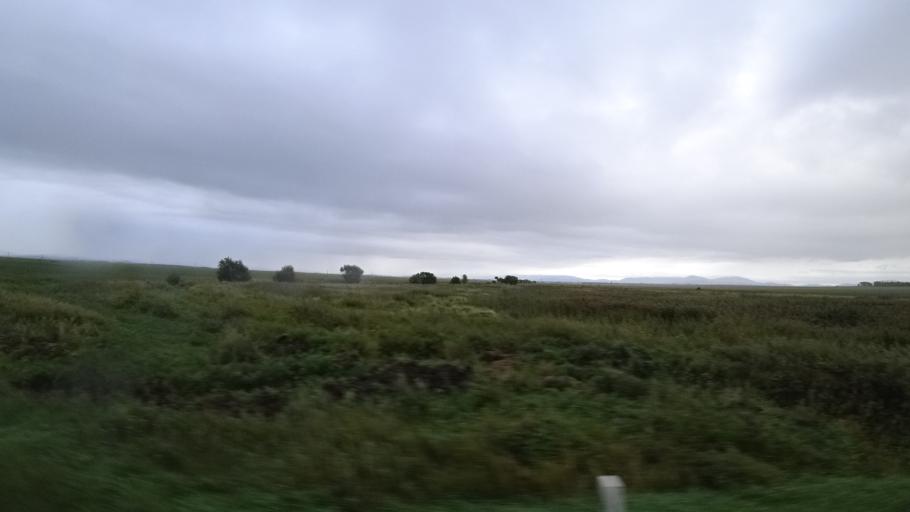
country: RU
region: Primorskiy
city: Chernigovka
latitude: 44.3815
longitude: 132.5296
